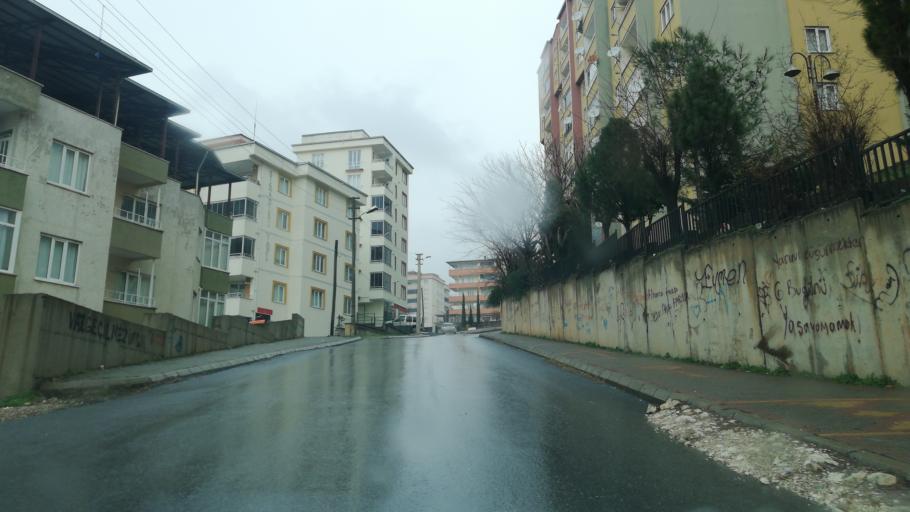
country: TR
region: Kahramanmaras
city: Kahramanmaras
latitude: 37.5933
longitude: 36.9012
